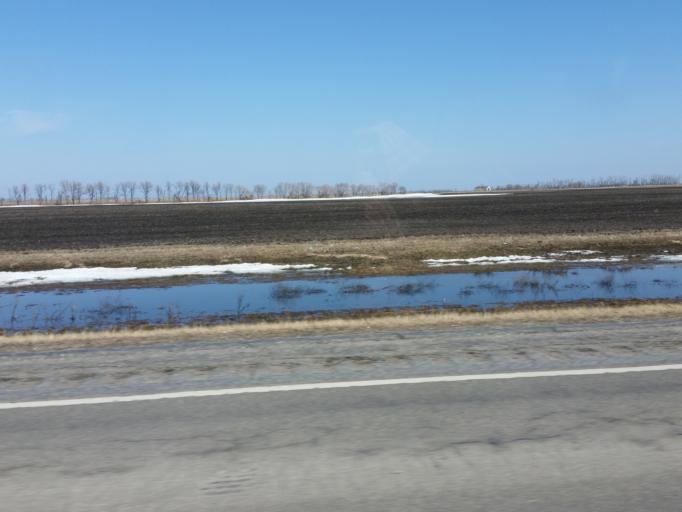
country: US
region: North Dakota
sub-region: Walsh County
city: Grafton
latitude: 48.3011
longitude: -97.3797
